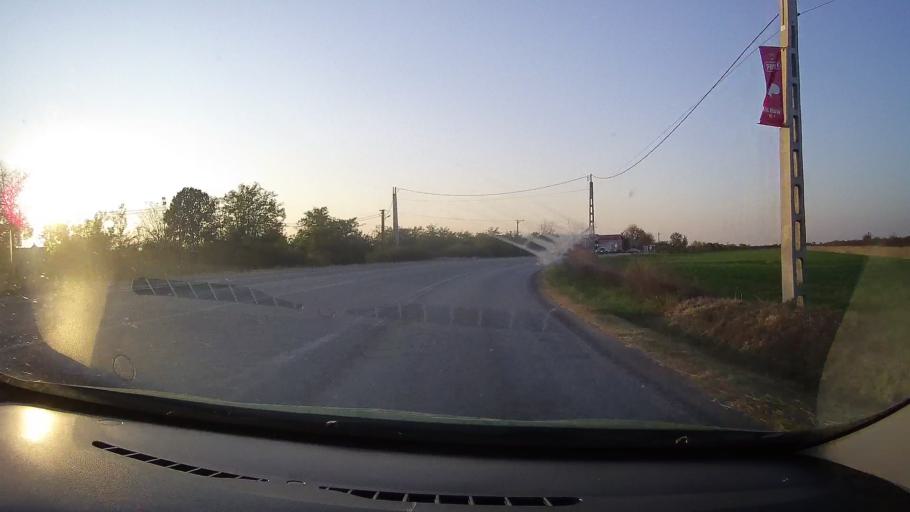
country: RO
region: Arad
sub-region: Comuna Ineu
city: Ineu
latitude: 46.4287
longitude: 21.8611
